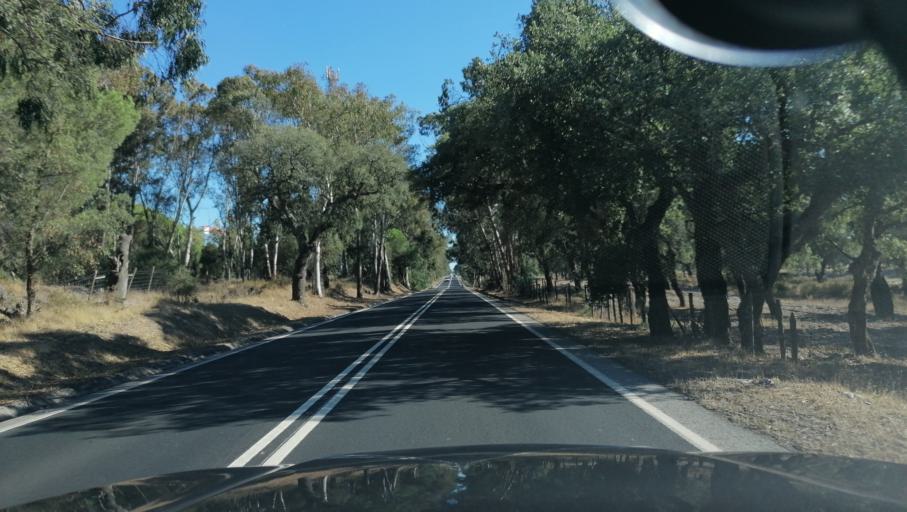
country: PT
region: Santarem
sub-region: Benavente
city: Poceirao
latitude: 38.8368
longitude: -8.8810
